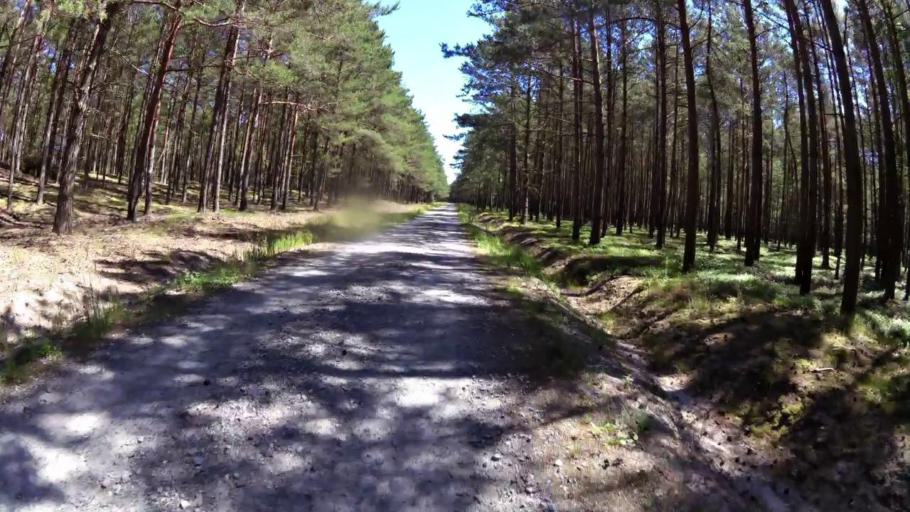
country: PL
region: West Pomeranian Voivodeship
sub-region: Powiat gryficki
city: Trzebiatow
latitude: 54.1041
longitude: 15.1775
